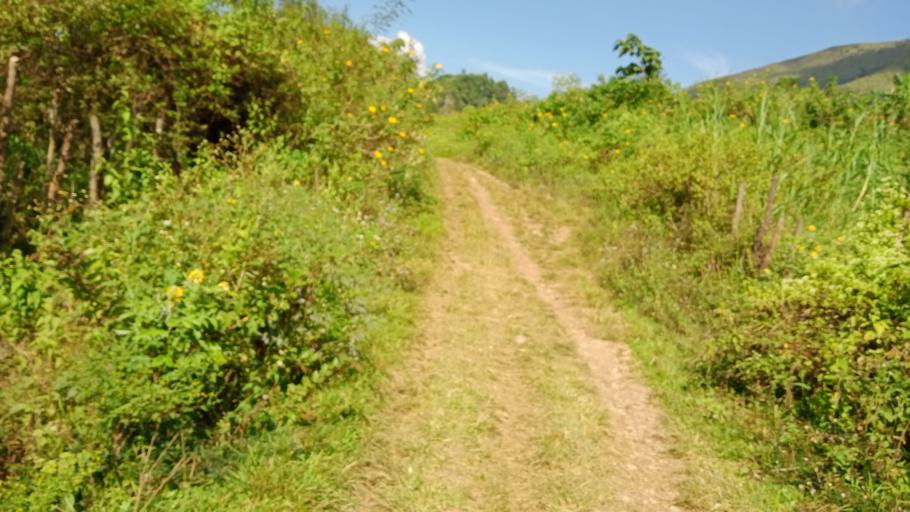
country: LA
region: Xiangkhoang
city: Phonsavan
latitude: 19.1105
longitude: 102.9290
